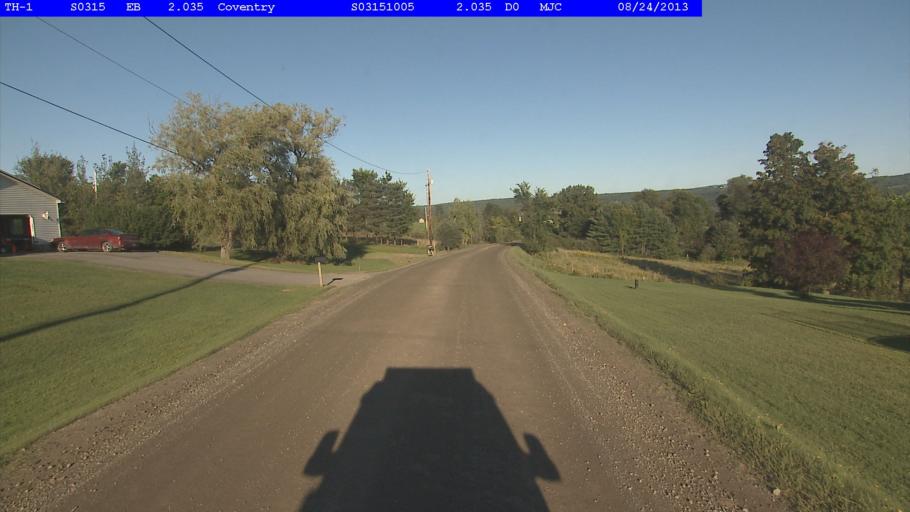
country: US
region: Vermont
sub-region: Orleans County
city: Newport
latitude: 44.8717
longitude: -72.2216
